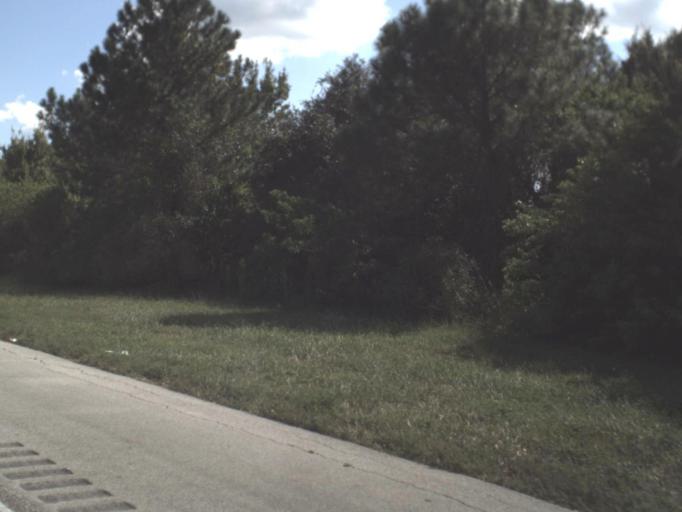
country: US
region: Florida
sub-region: Osceola County
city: Saint Cloud
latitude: 28.0387
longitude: -81.2040
